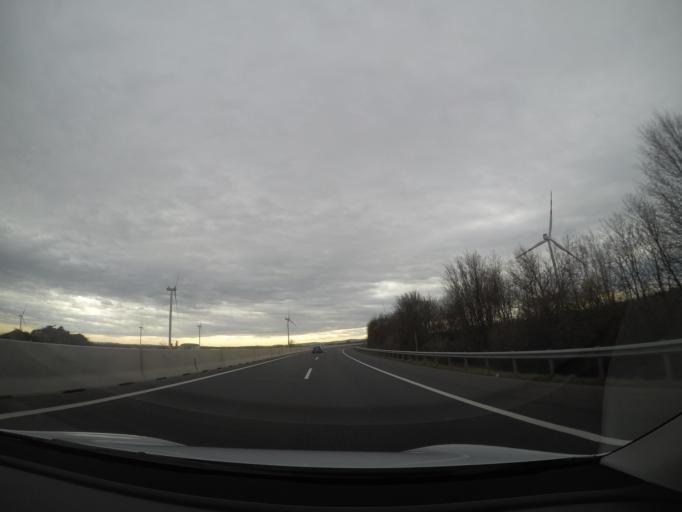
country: AT
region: Lower Austria
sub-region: Politischer Bezirk Modling
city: Munchendorf
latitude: 48.0054
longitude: 16.3812
